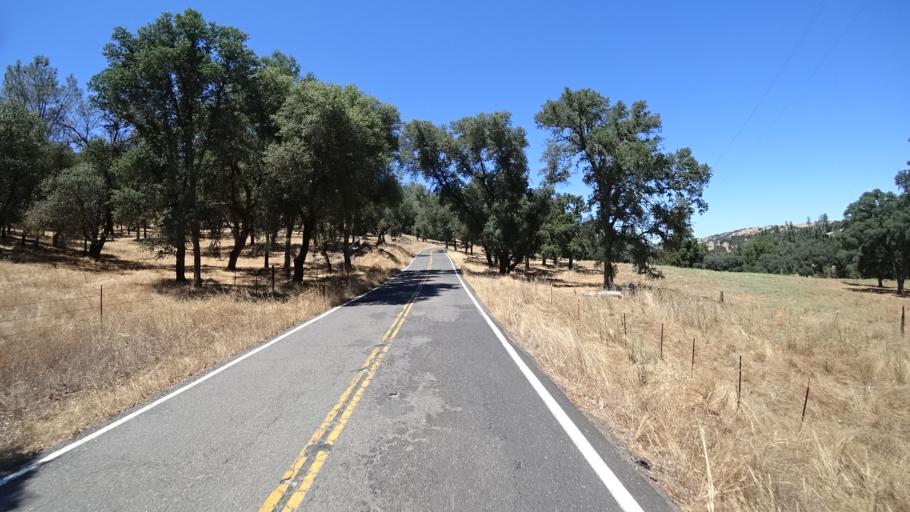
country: US
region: California
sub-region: Calaveras County
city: San Andreas
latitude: 38.1294
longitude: -120.6629
